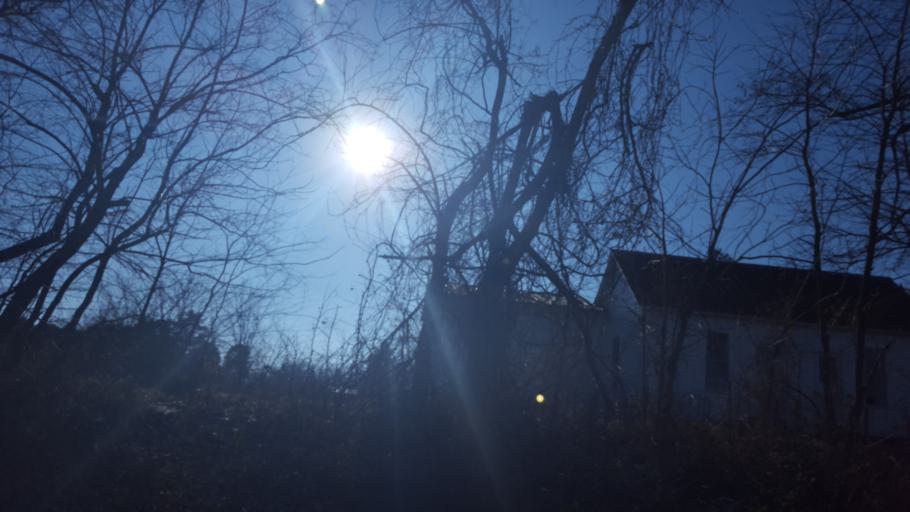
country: US
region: Kentucky
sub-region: Crittenden County
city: Marion
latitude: 37.4031
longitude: -88.0223
